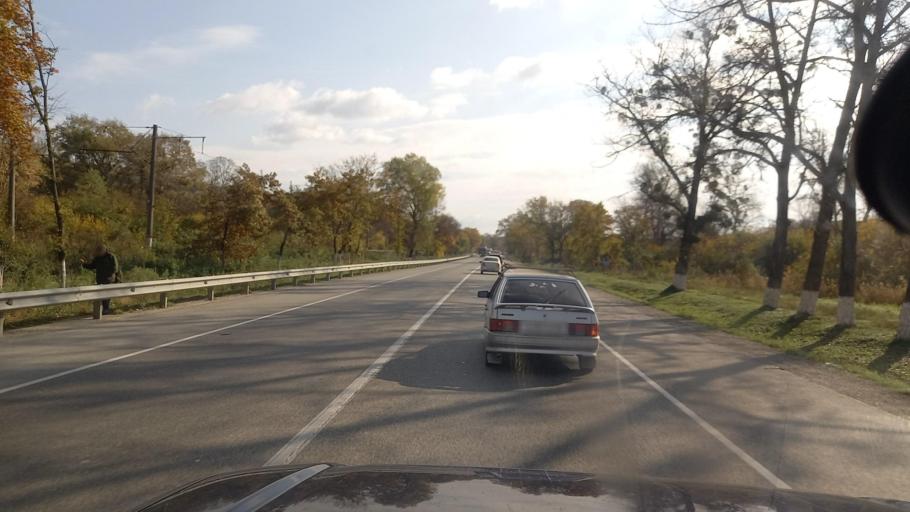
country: RU
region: Krasnodarskiy
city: Gayduk
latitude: 44.8721
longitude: 37.8352
